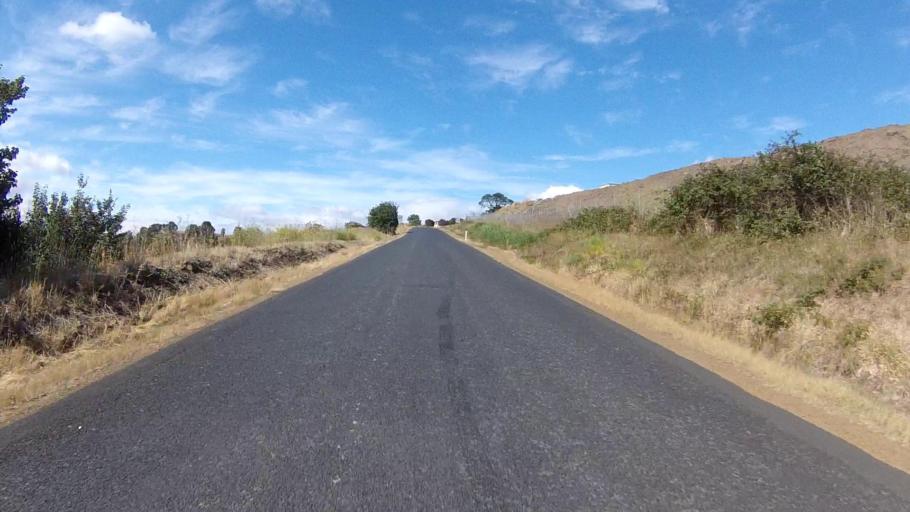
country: AU
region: Tasmania
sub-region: Brighton
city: Bridgewater
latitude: -42.7338
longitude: 147.2602
